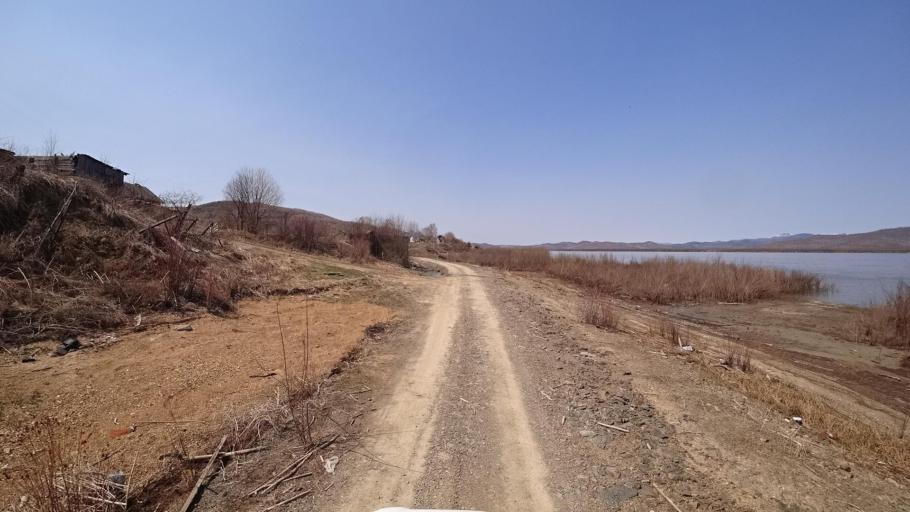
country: RU
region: Khabarovsk Krai
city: Selikhino
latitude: 50.6682
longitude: 137.4034
